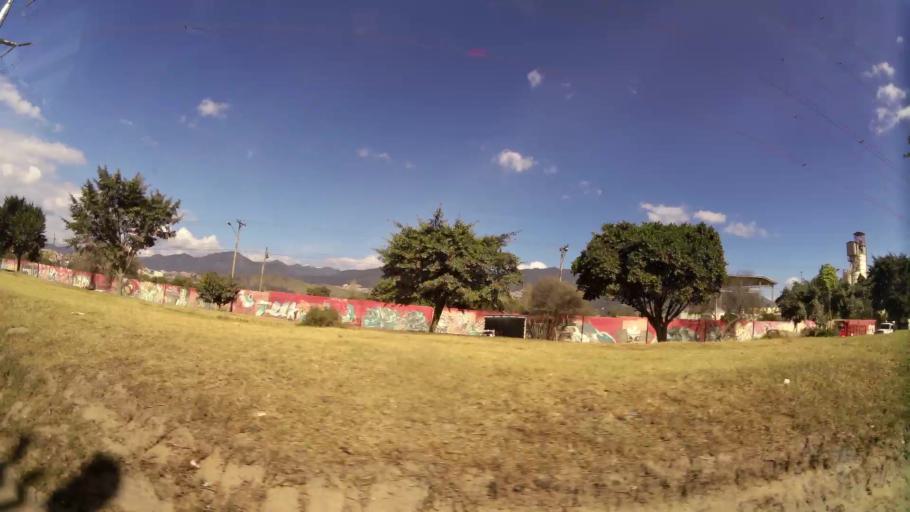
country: CO
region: Bogota D.C.
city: Bogota
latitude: 4.5488
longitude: -74.1370
